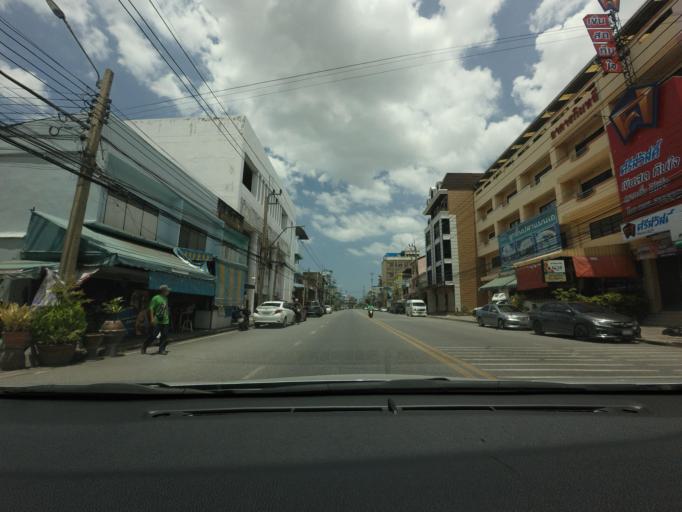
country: TH
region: Samut Prakan
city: Samut Prakan
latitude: 13.5866
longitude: 100.5958
